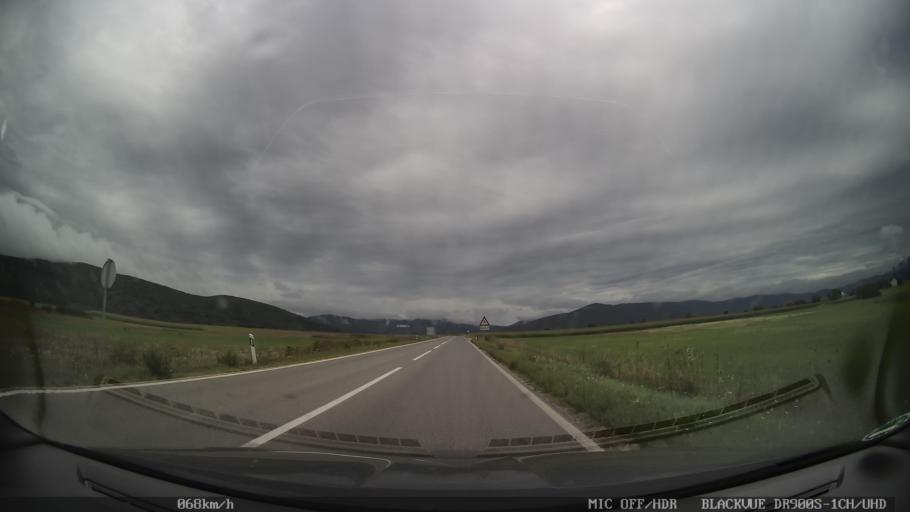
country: HR
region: Licko-Senjska
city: Otocac
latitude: 44.8560
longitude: 15.2744
